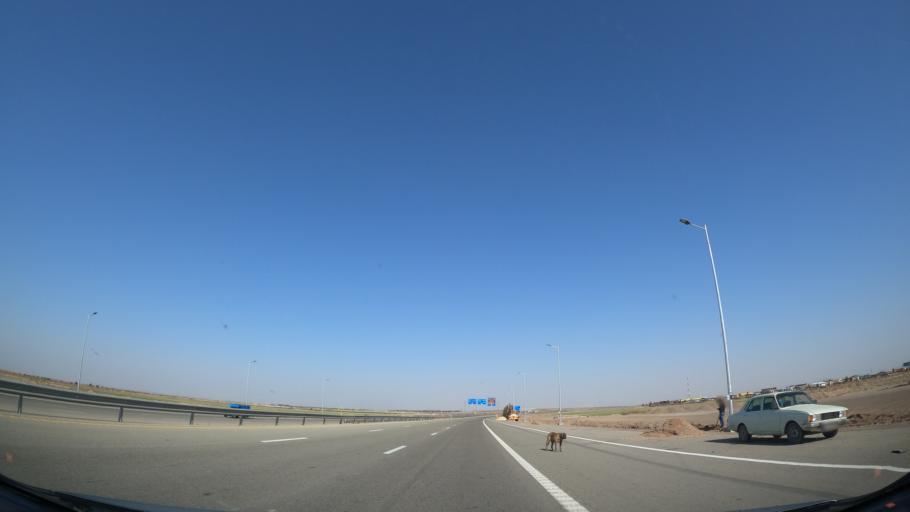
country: IR
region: Tehran
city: Eqbaliyeh
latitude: 35.1388
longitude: 51.5243
